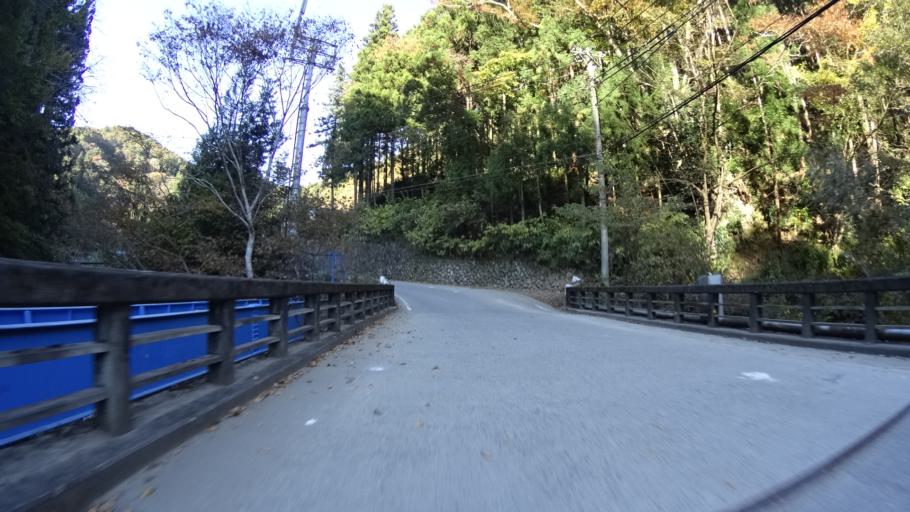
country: JP
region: Yamanashi
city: Uenohara
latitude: 35.6390
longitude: 139.1399
